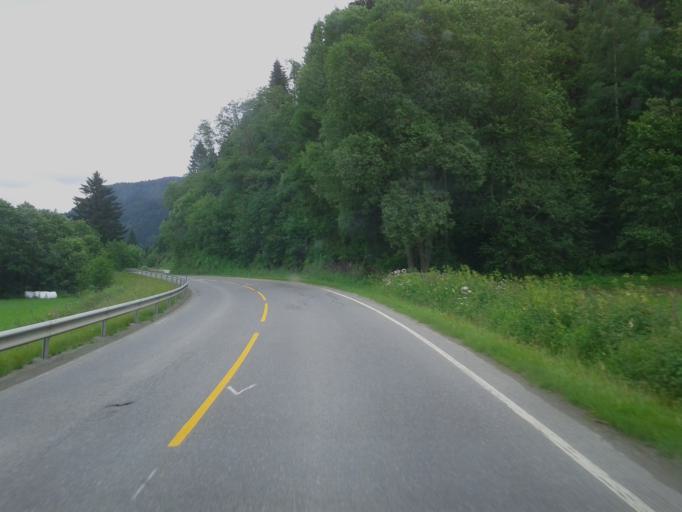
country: NO
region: Sor-Trondelag
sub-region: Midtre Gauldal
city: Storen
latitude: 63.0168
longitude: 10.3381
